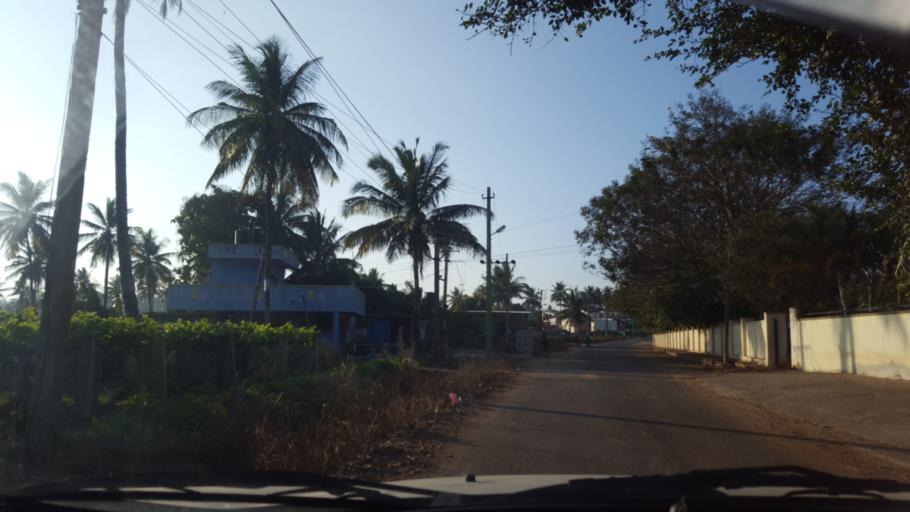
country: IN
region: Karnataka
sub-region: Bangalore Urban
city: Yelahanka
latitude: 13.1764
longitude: 77.5910
